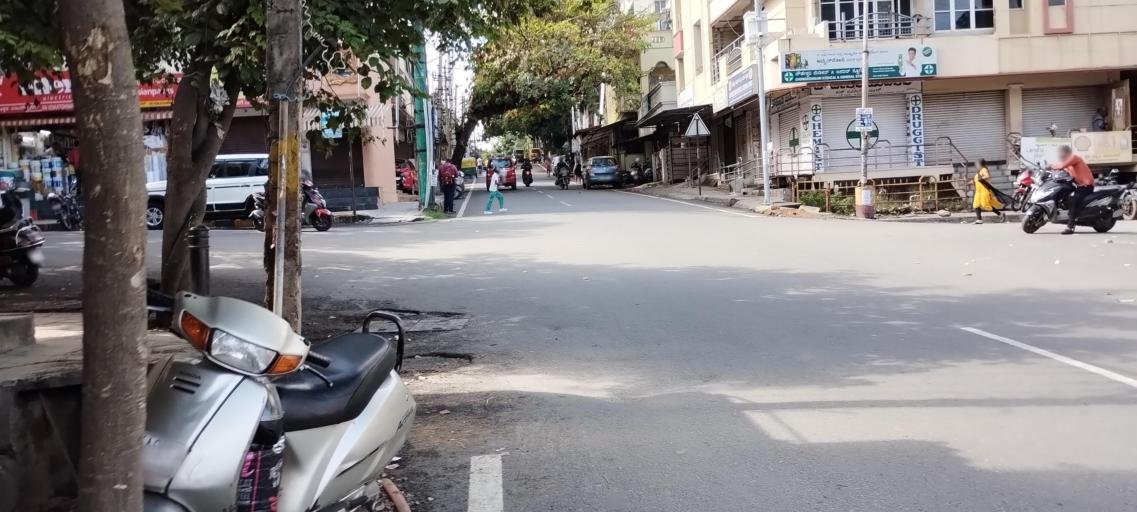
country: IN
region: Karnataka
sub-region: Bangalore Urban
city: Bangalore
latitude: 12.9412
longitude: 77.5388
